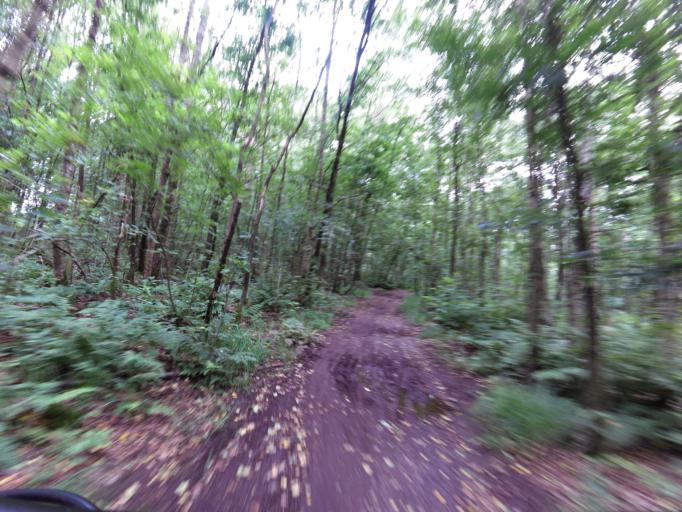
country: NL
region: North Brabant
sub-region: Gemeente Son en Breugel
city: Breugel
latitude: 51.5521
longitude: 5.5220
